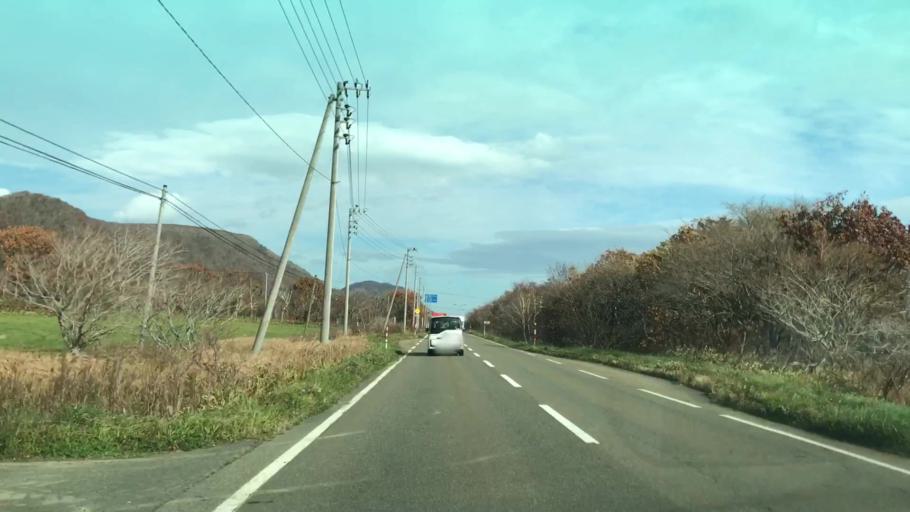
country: JP
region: Hokkaido
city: Obihiro
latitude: 42.0188
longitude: 143.2563
